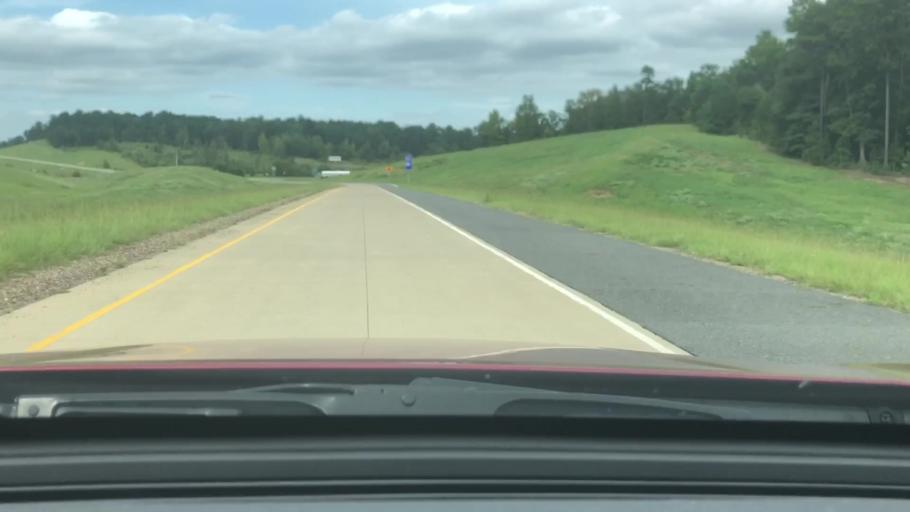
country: US
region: Louisiana
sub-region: Caddo Parish
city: Vivian
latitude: 32.9402
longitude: -93.8968
